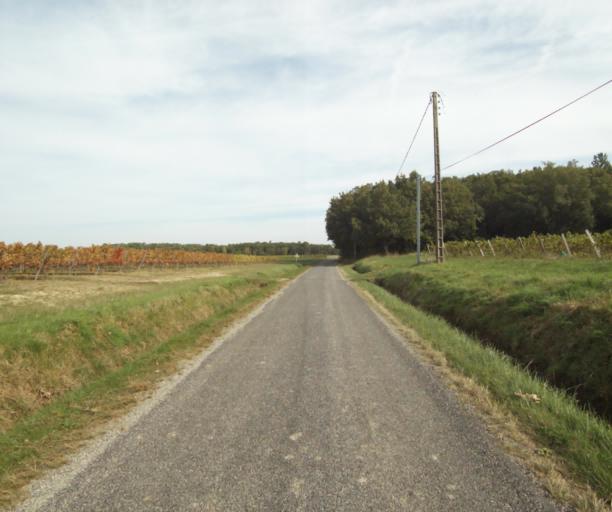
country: FR
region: Midi-Pyrenees
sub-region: Departement du Tarn-et-Garonne
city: Labastide-Saint-Pierre
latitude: 43.8786
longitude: 1.3652
